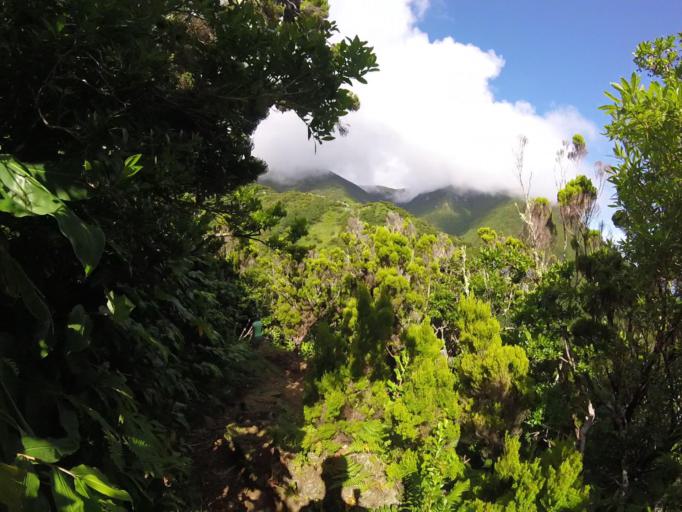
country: PT
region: Azores
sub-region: Sao Roque do Pico
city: Sao Roque do Pico
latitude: 38.6073
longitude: -27.9205
